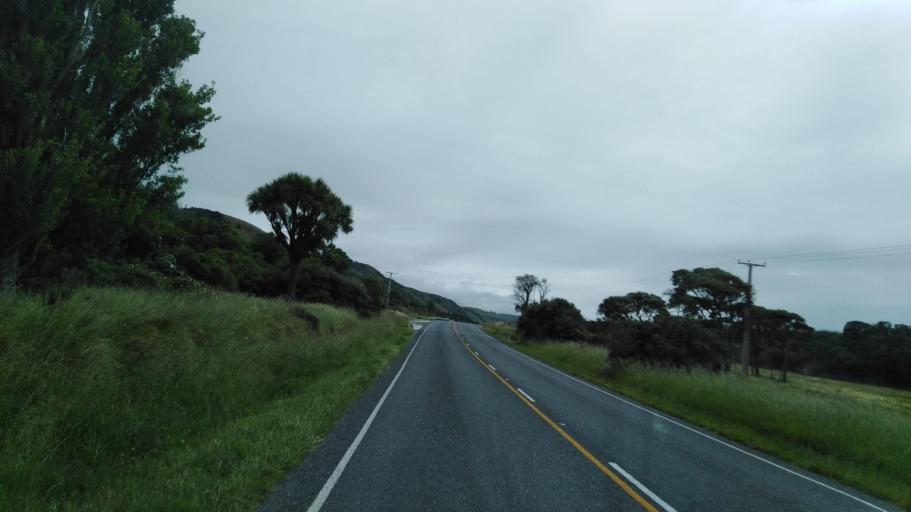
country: NZ
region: Canterbury
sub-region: Kaikoura District
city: Kaikoura
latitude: -42.1188
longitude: 173.9229
